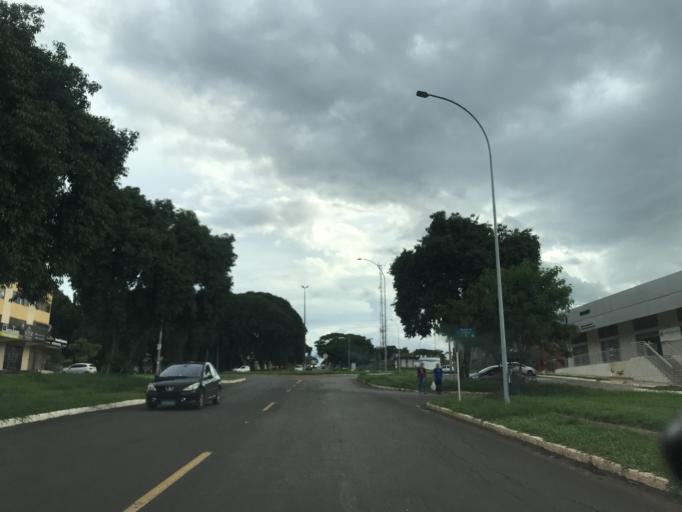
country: BR
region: Federal District
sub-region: Brasilia
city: Brasilia
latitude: -15.6440
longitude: -47.7931
